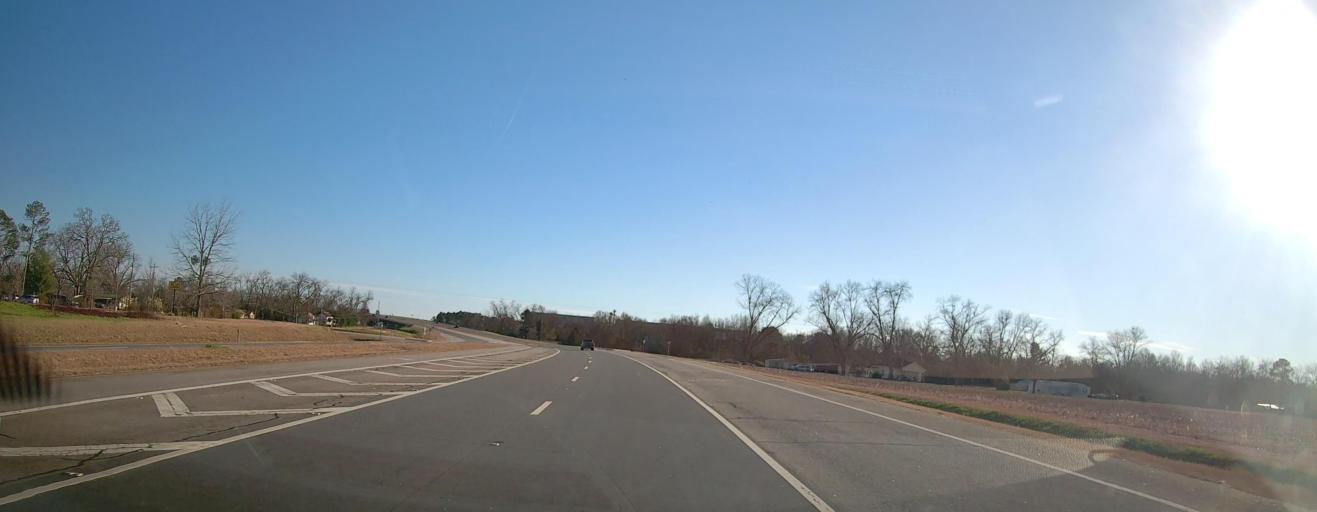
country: US
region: Georgia
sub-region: Sumter County
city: Americus
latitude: 31.9028
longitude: -84.2626
